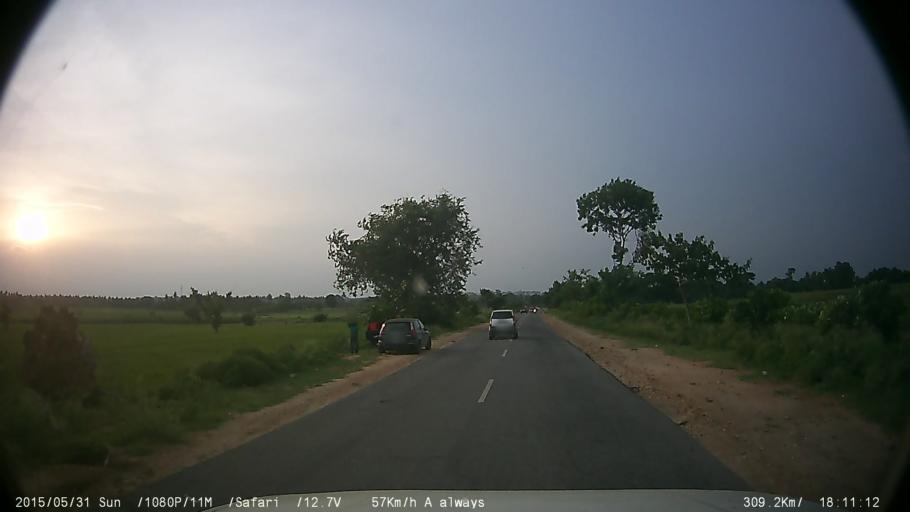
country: IN
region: Karnataka
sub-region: Mysore
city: Nanjangud
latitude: 12.0855
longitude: 76.6749
